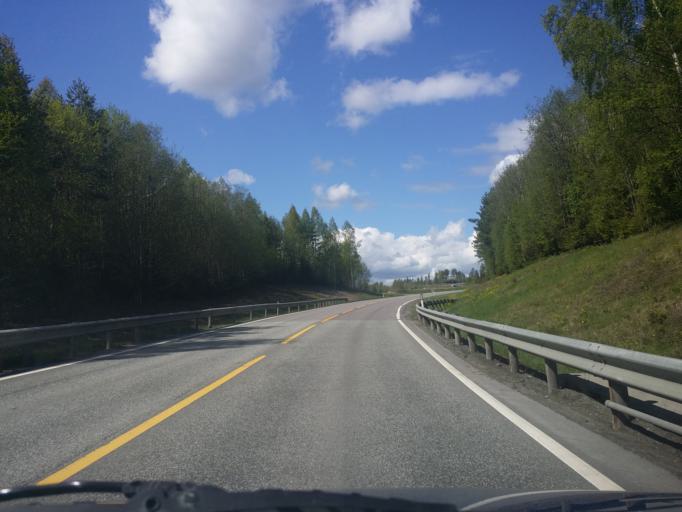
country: NO
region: Buskerud
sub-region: Ringerike
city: Honefoss
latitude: 60.1463
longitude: 10.2302
